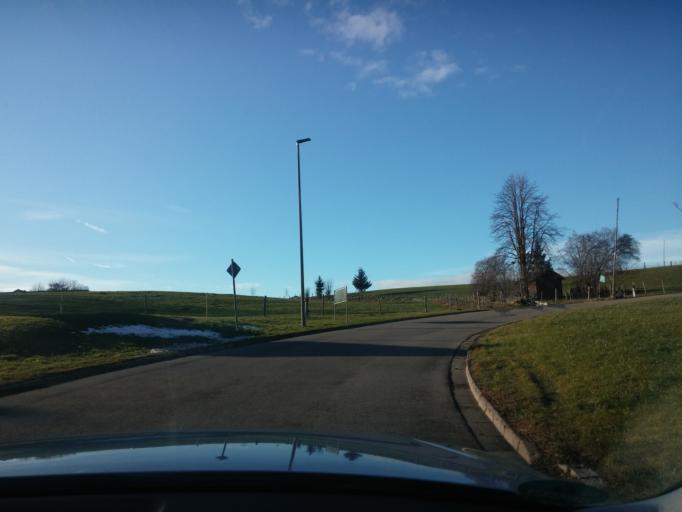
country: DE
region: Bavaria
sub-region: Swabia
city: Lautrach
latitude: 47.8898
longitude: 10.1360
